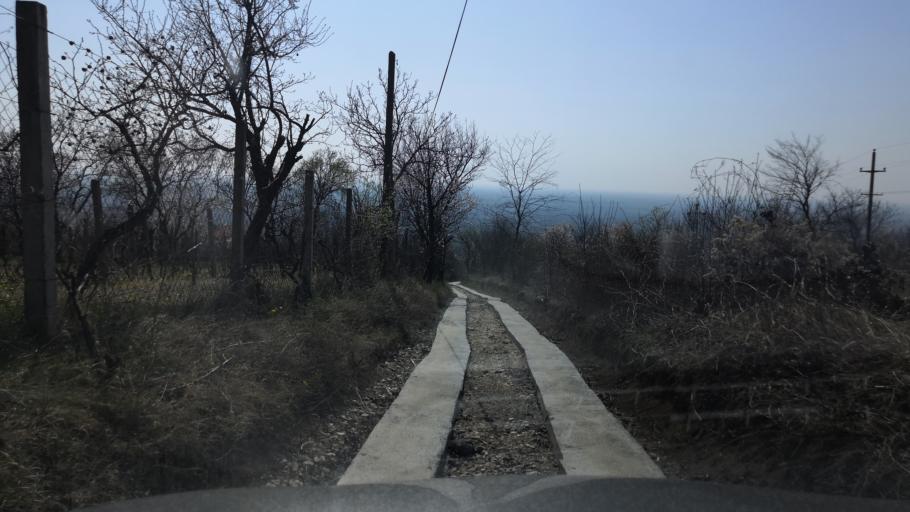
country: RS
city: Krcedin
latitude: 45.1612
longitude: 20.1867
